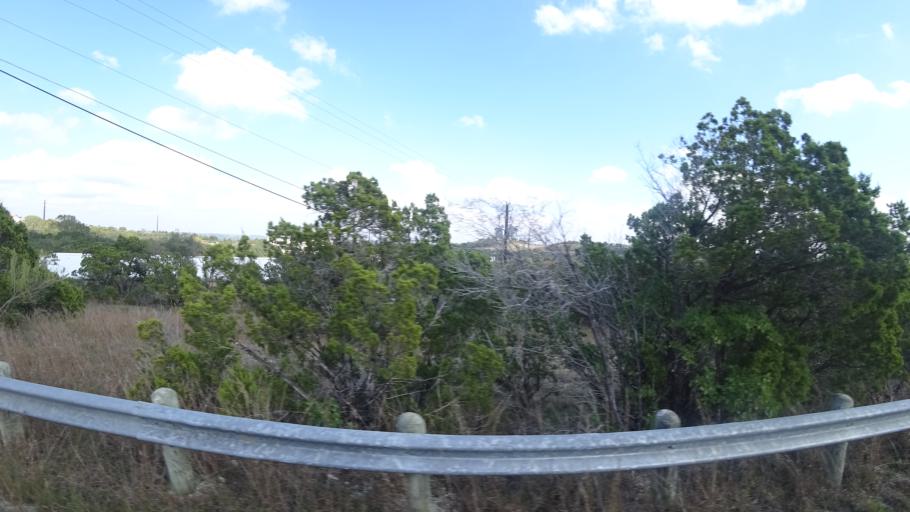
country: US
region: Texas
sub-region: Travis County
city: Lost Creek
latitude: 30.3151
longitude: -97.8642
